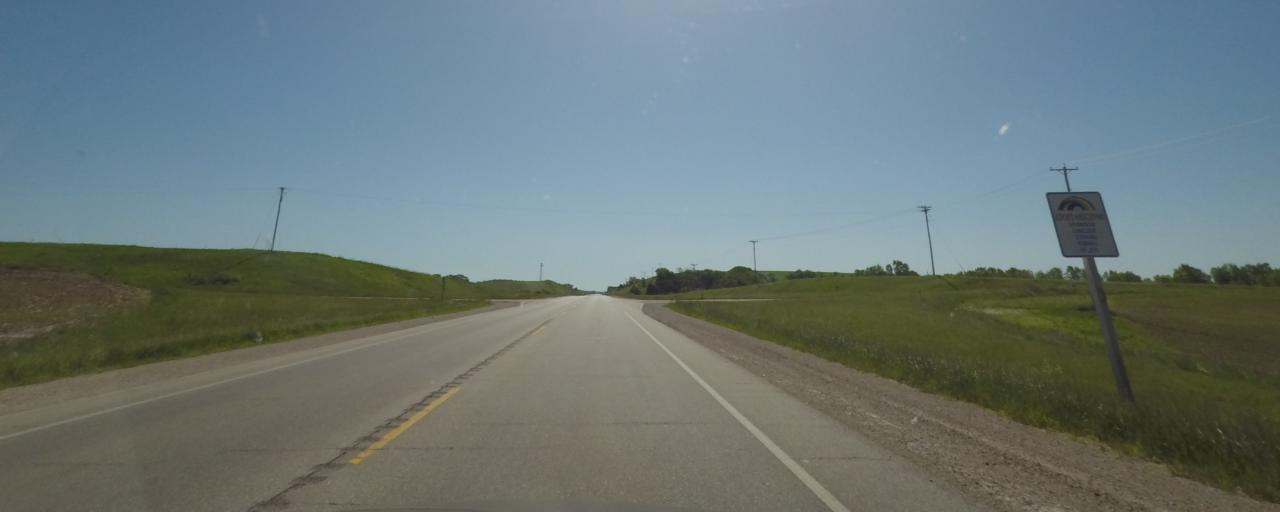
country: US
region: Wisconsin
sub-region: Fond du Lac County
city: Saint Peter
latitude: 43.7833
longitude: -88.3228
